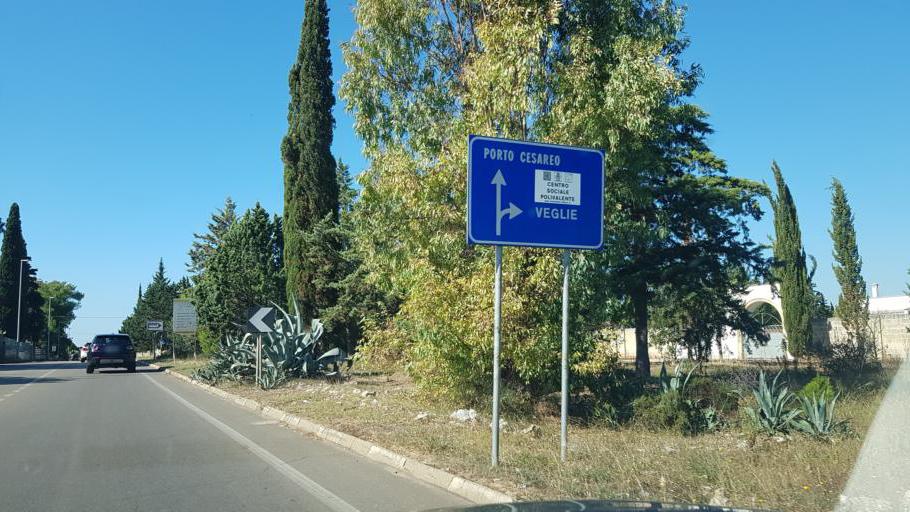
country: IT
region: Apulia
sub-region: Provincia di Lecce
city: Leverano
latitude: 40.2862
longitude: 17.9673
